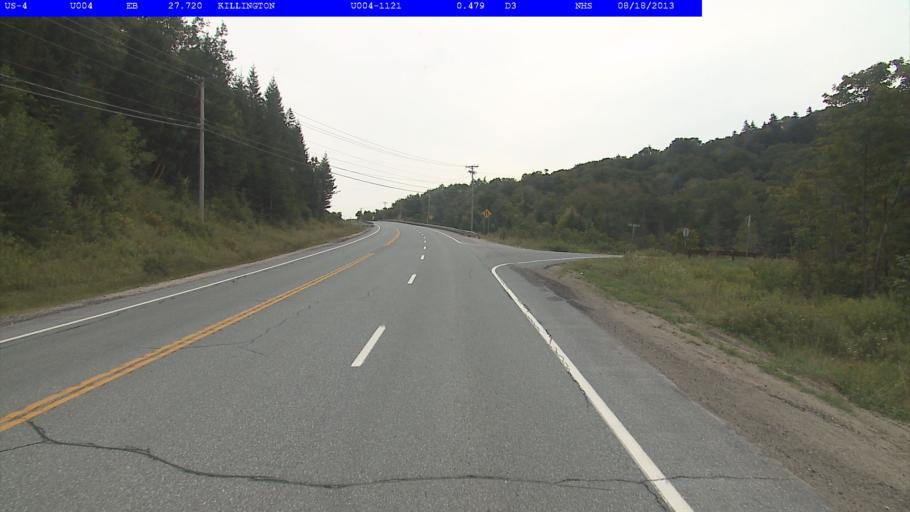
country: US
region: Vermont
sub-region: Rutland County
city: Rutland
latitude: 43.6636
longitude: -72.8372
